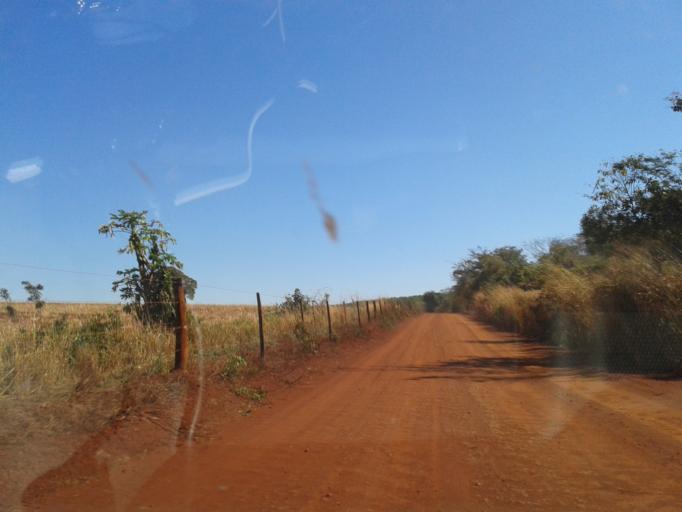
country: BR
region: Minas Gerais
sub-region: Centralina
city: Centralina
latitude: -18.5778
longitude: -49.1334
